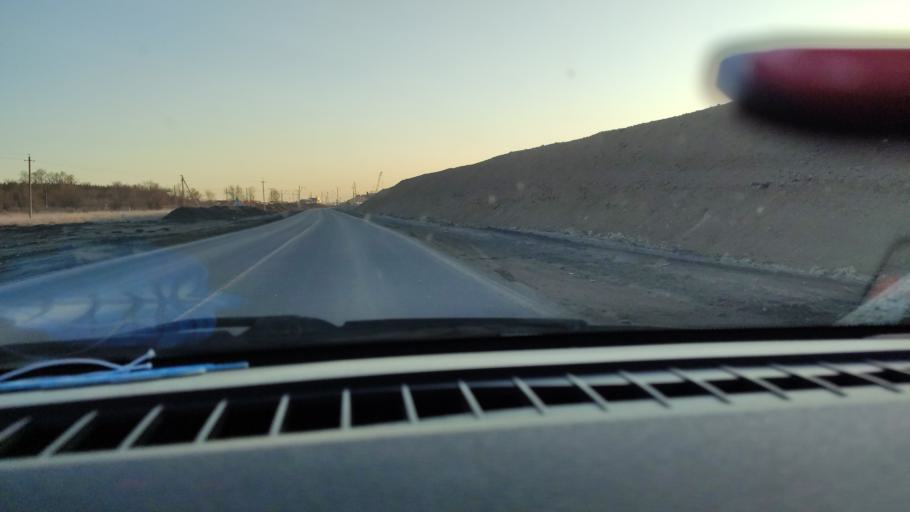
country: RU
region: Saratov
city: Sinodskoye
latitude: 52.0076
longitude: 46.6850
